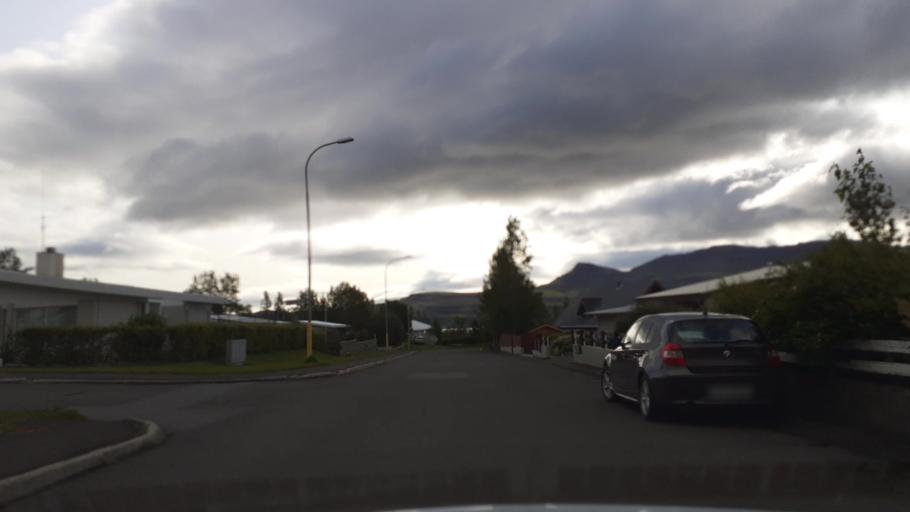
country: IS
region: East
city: Neskaupstadur
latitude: 65.1492
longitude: -13.6728
